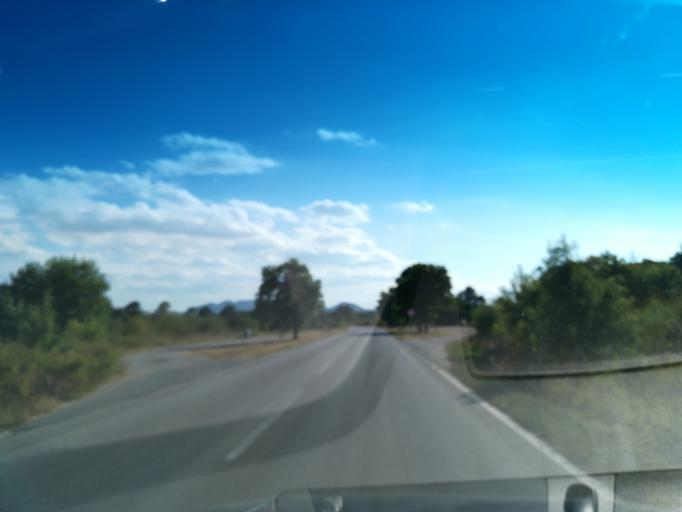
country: BG
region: Khaskovo
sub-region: Obshtina Mineralni Bani
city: Mineralni Bani
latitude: 41.9884
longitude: 25.3542
